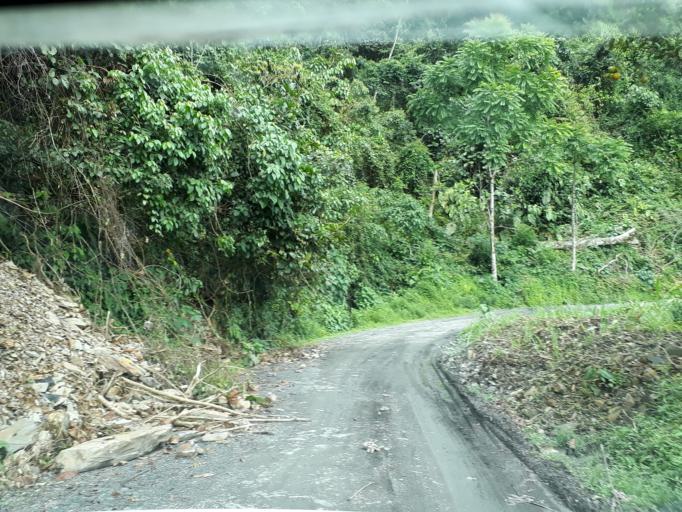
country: CO
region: Boyaca
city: Quipama
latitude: 5.4178
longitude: -74.1863
